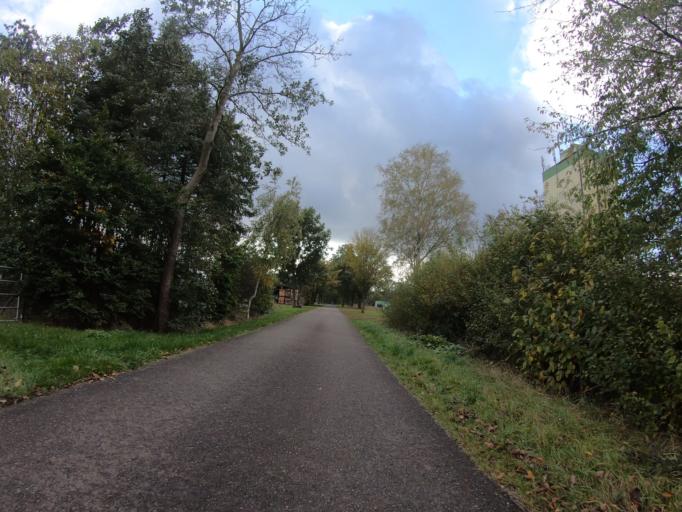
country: DE
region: Lower Saxony
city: Wahrenholz
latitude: 52.6048
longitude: 10.6076
